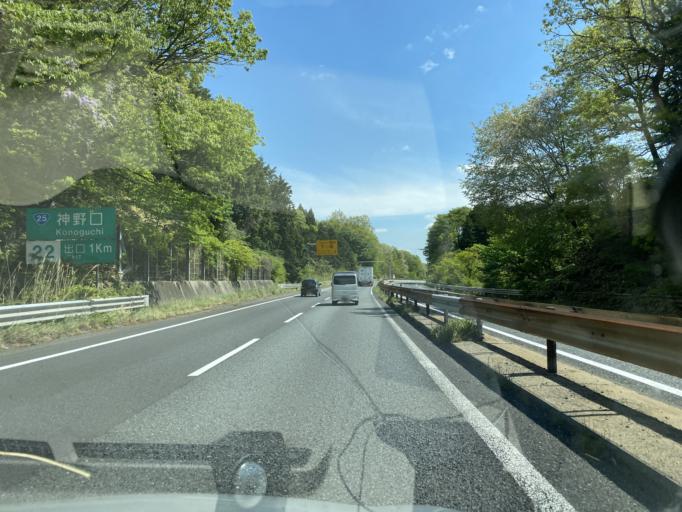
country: JP
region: Mie
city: Nabari
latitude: 34.6429
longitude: 136.0086
